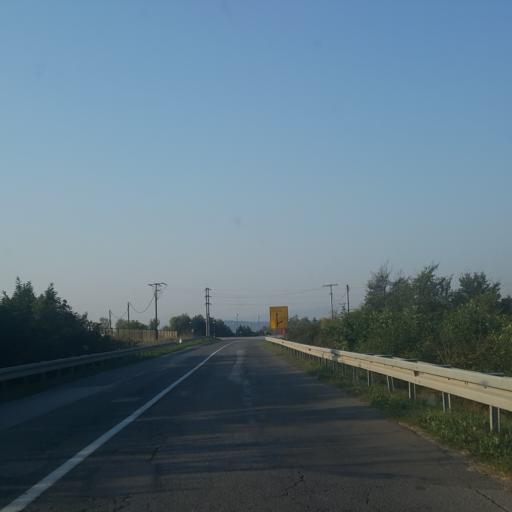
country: RS
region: Central Serbia
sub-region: Zajecarski Okrug
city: Zajecar
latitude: 43.9282
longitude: 22.2986
